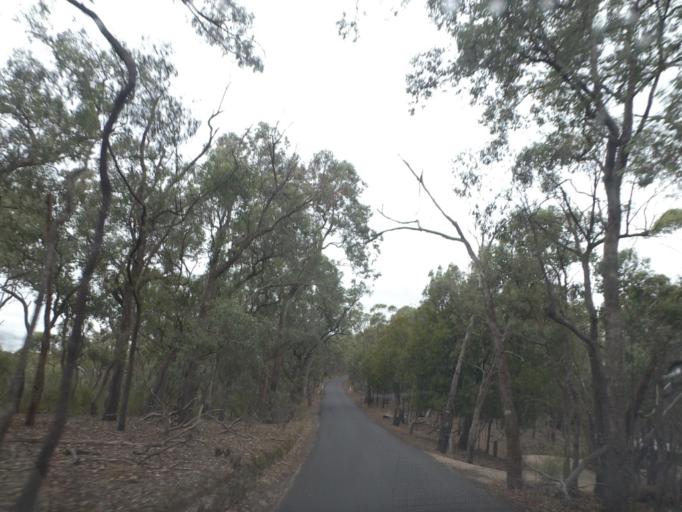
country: AU
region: Victoria
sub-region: Yarra Ranges
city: Chirnside Park
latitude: -37.6962
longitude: 145.2775
